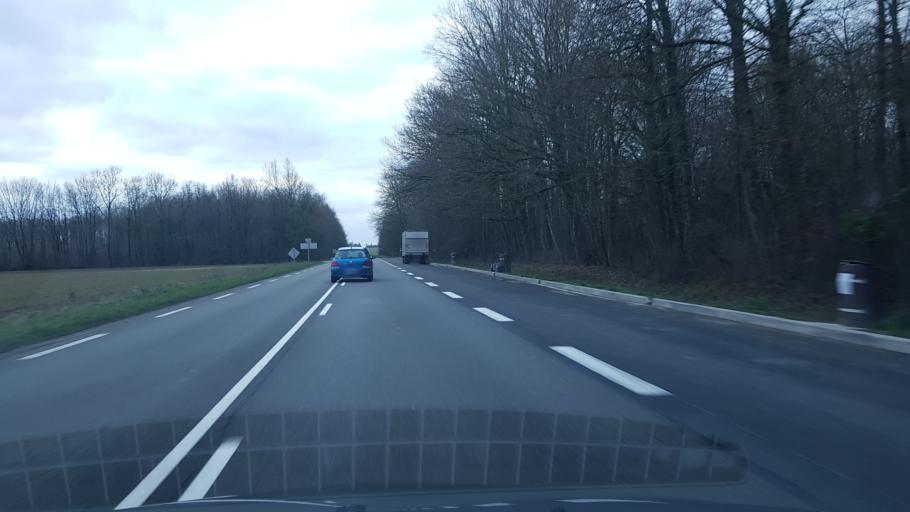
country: FR
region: Ile-de-France
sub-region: Departement de Seine-et-Marne
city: Villiers-Saint-Georges
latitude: 48.7071
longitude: 3.4671
